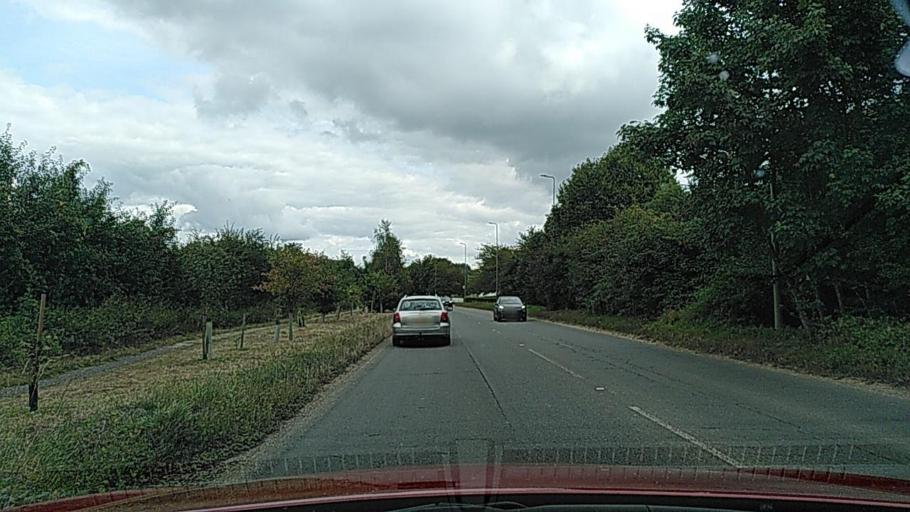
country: GB
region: England
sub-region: Wokingham
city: Sonning
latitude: 51.4769
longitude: -0.9357
